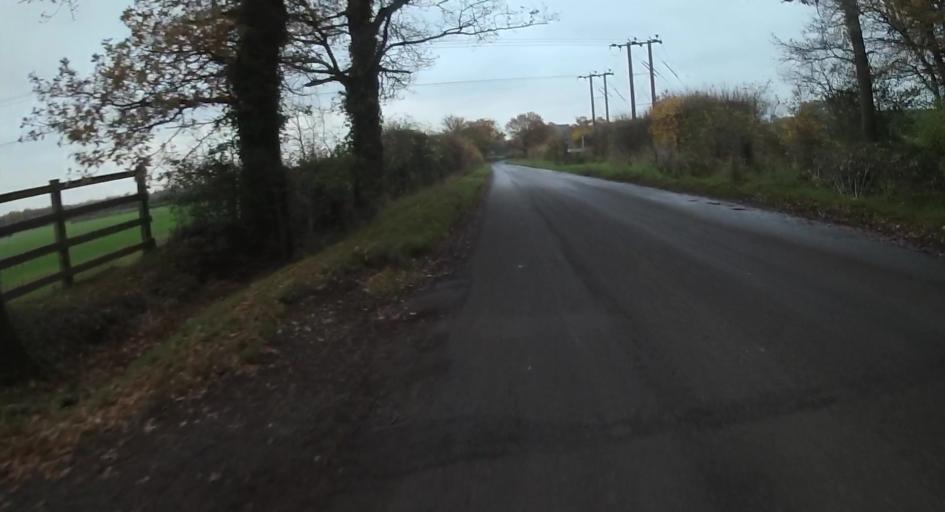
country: GB
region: England
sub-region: West Berkshire
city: Arborfield
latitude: 51.3866
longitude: -0.9264
